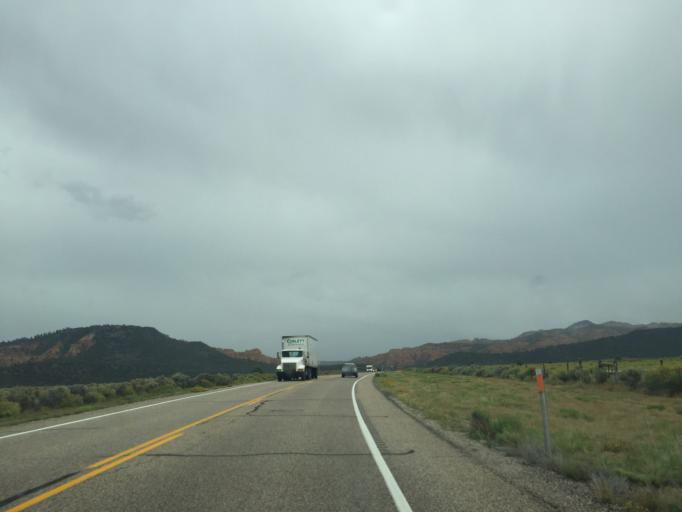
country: US
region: Utah
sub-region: Garfield County
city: Panguitch
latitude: 37.7485
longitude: -112.3605
